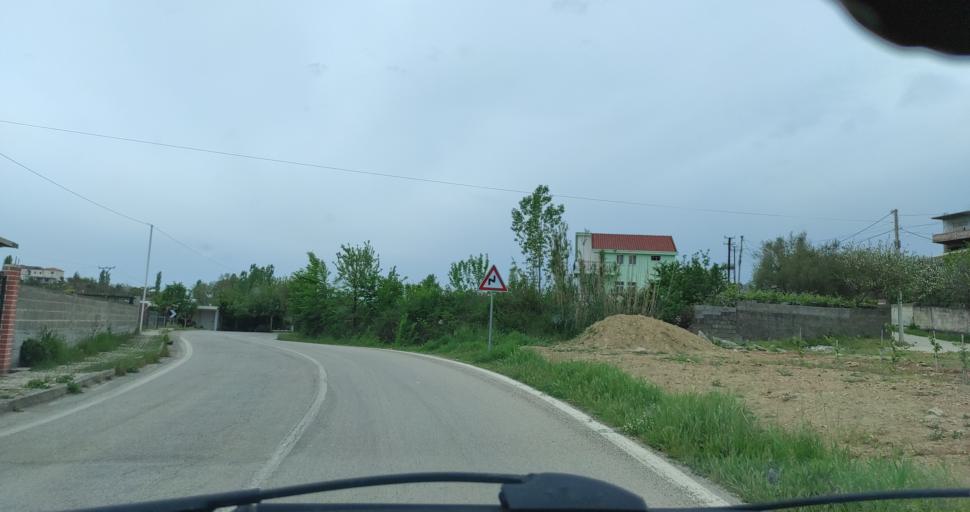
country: AL
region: Lezhe
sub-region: Rrethi i Kurbinit
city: Lac
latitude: 41.6166
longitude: 19.7118
